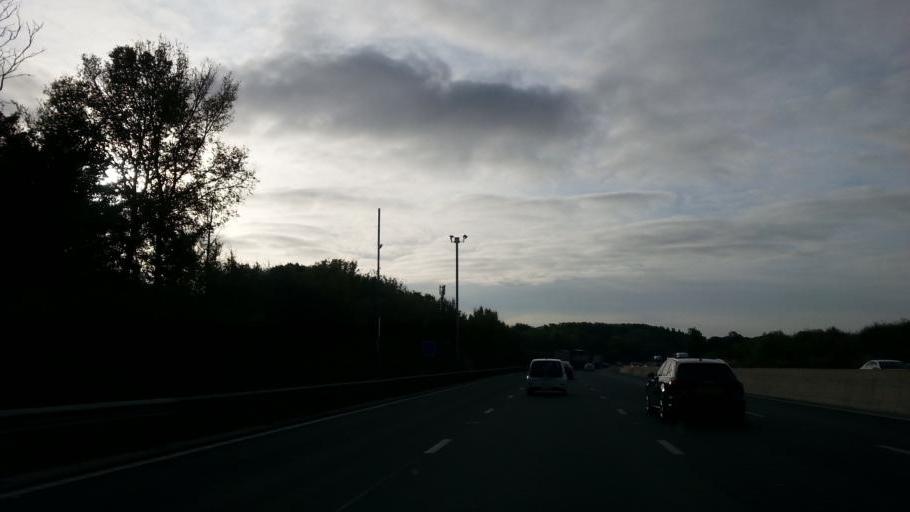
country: GB
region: England
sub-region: Northamptonshire
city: Long Buckby
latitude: 52.2794
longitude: -1.0963
